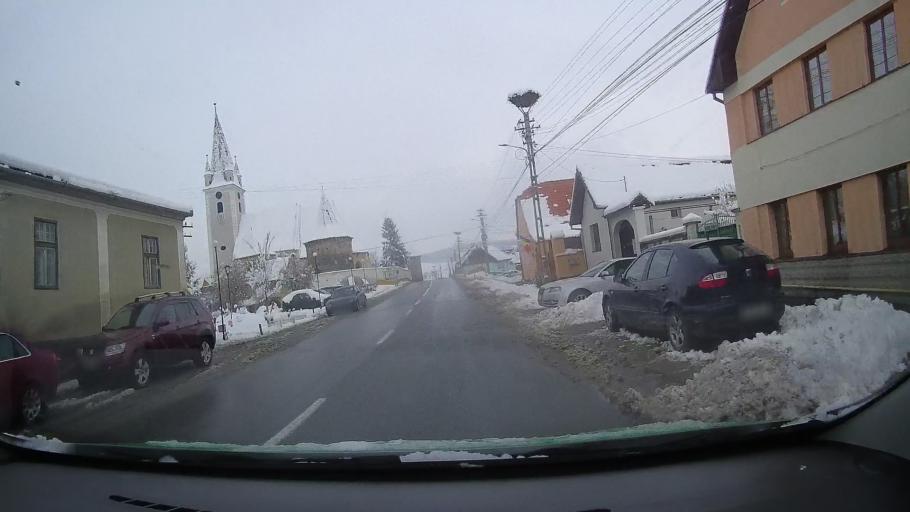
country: RO
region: Sibiu
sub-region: Comuna Cristian
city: Cristian
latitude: 45.7835
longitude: 24.0285
